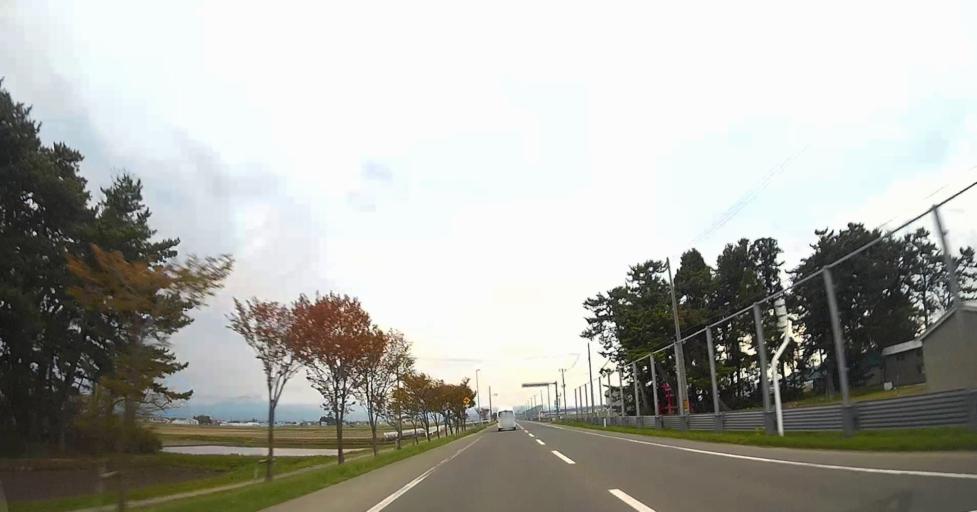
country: JP
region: Aomori
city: Aomori Shi
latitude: 40.8970
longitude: 140.6678
